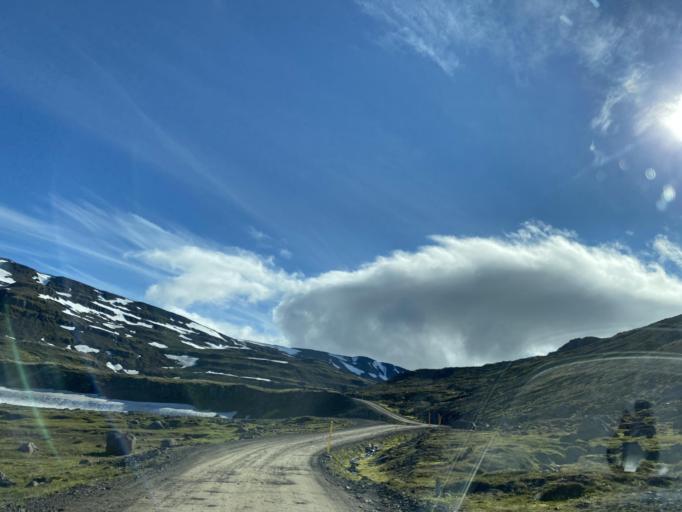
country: IS
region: East
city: Eskifjoerdur
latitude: 65.1731
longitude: -14.1173
